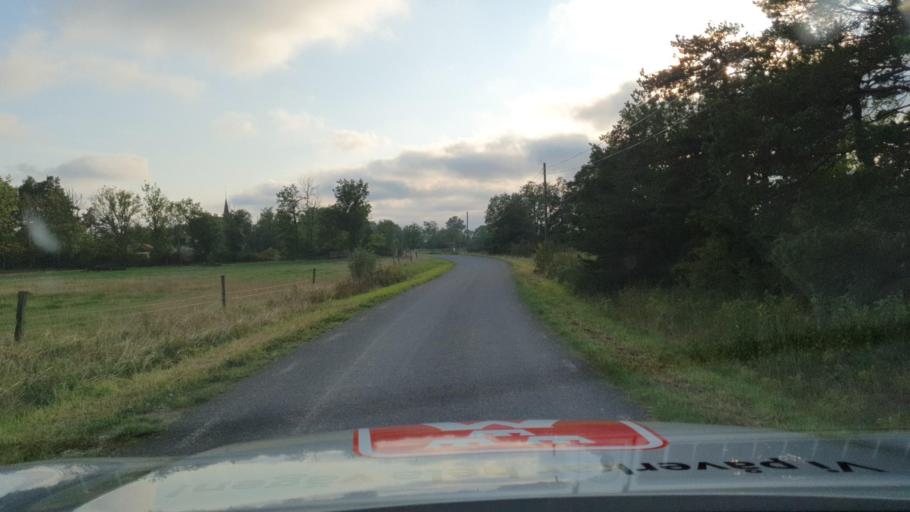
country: SE
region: Gotland
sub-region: Gotland
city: Klintehamn
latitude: 57.4430
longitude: 18.1556
